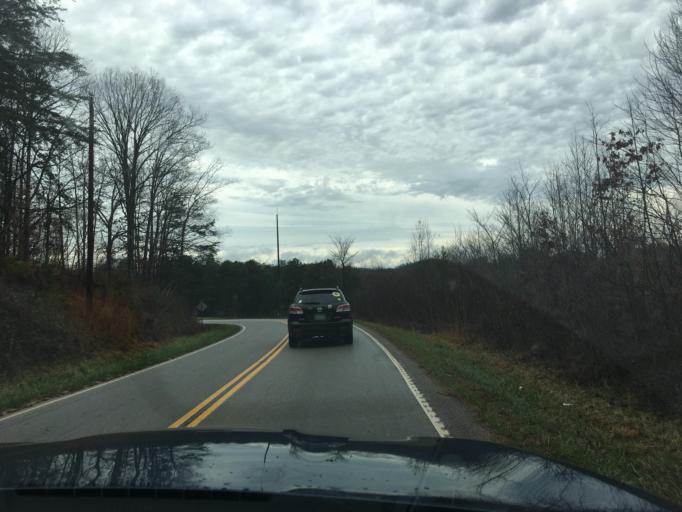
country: US
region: Tennessee
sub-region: McMinn County
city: Englewood
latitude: 35.3454
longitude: -84.3967
